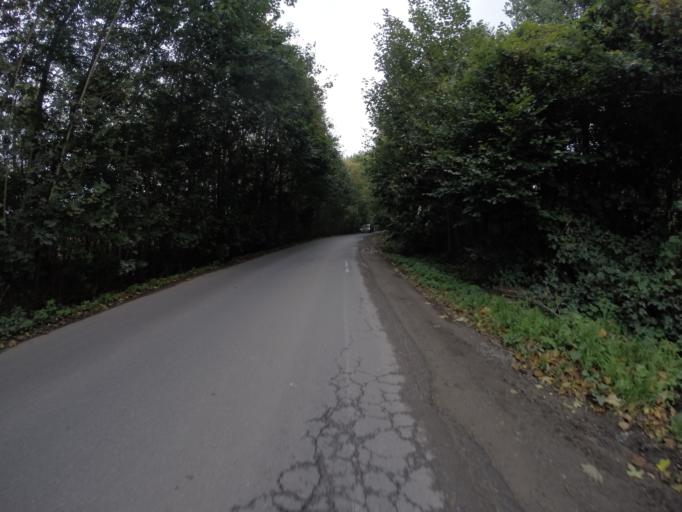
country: BE
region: Flanders
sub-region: Provincie Oost-Vlaanderen
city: Aalter
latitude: 51.1003
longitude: 3.4140
